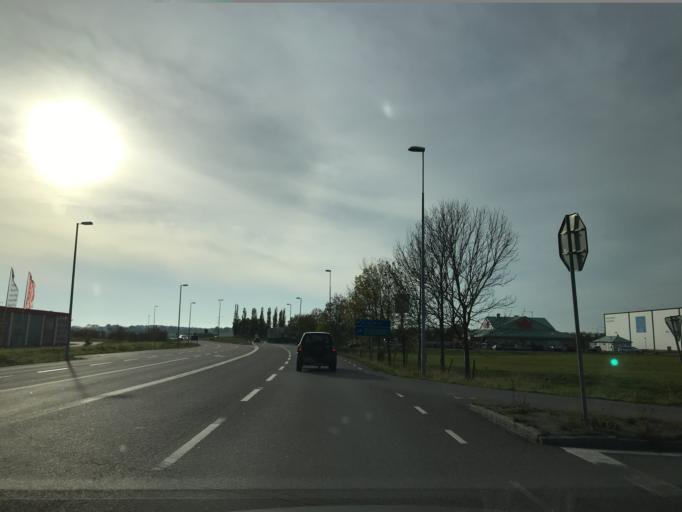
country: SE
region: Skane
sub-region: Helsingborg
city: Hyllinge
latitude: 56.1003
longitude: 12.8547
